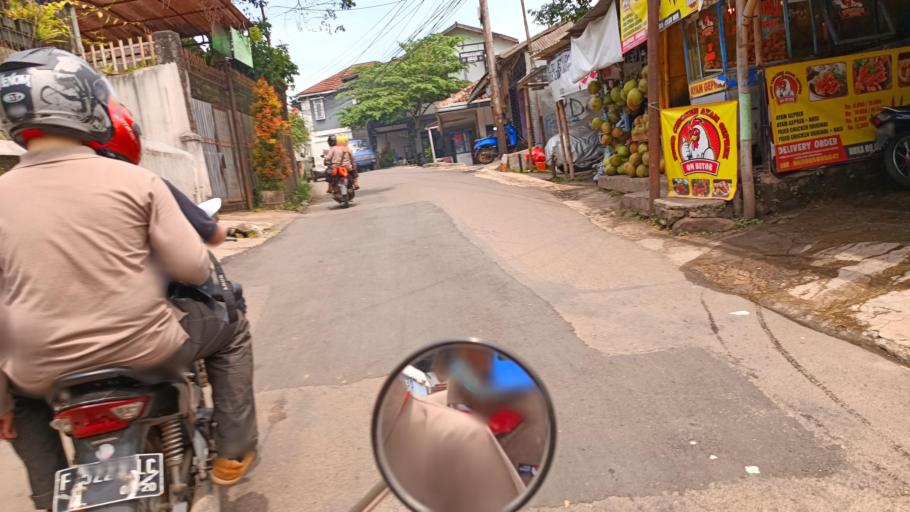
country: ID
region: West Java
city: Caringin
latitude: -6.6501
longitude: 106.9065
